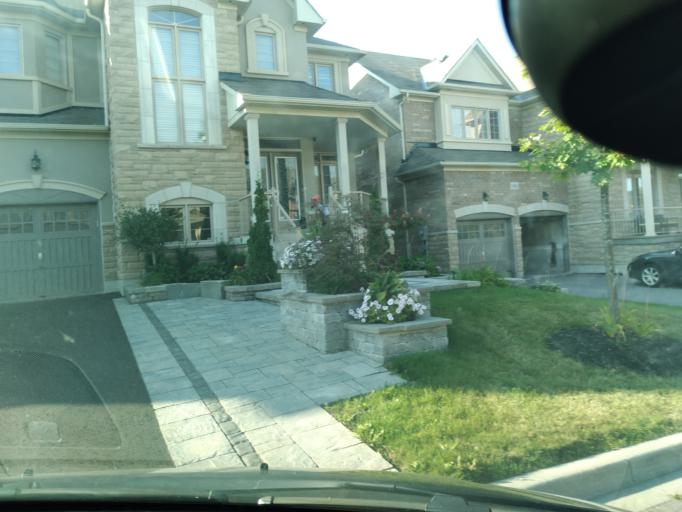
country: CA
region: Ontario
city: Newmarket
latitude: 44.0414
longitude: -79.4193
